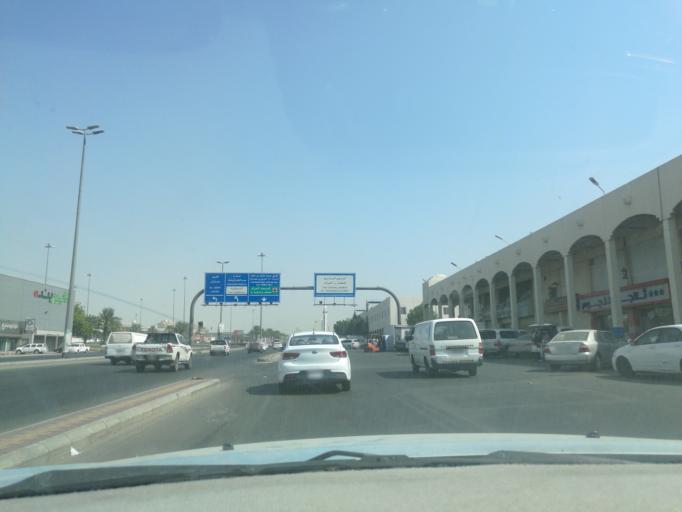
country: SA
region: Makkah
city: Mecca
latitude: 21.3680
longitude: 39.8040
